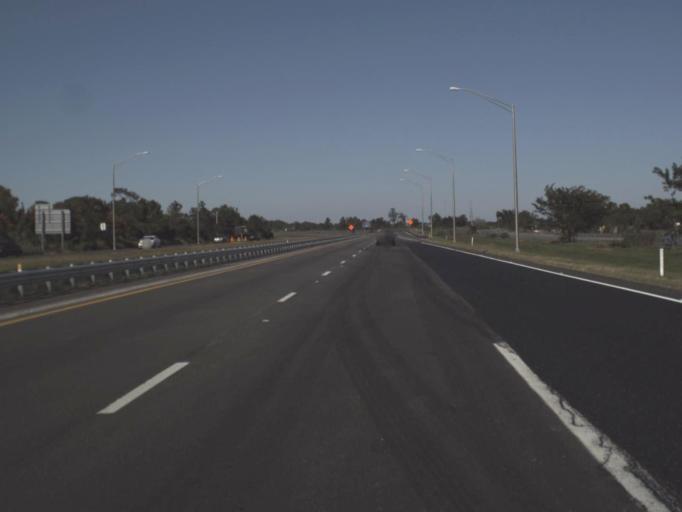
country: US
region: Florida
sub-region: Seminole County
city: Sanford
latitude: 28.7915
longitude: -81.3023
